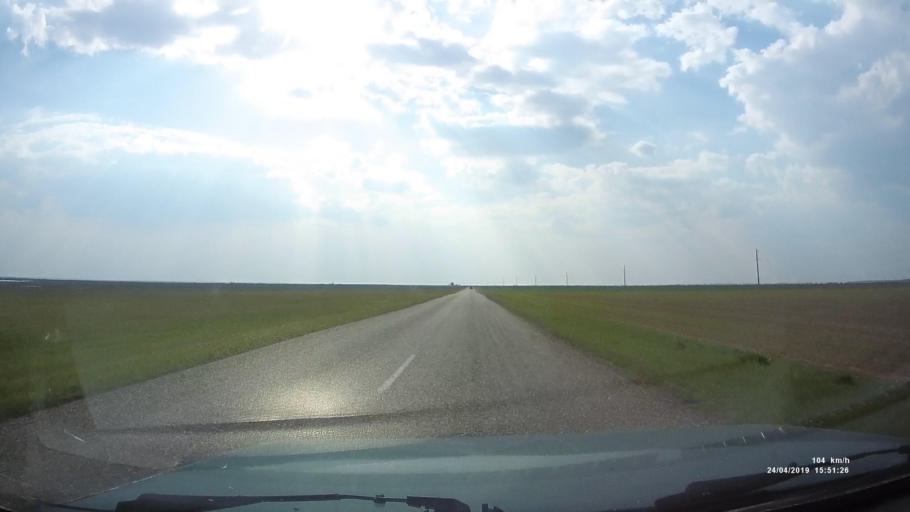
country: RU
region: Kalmykiya
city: Yashalta
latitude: 46.6044
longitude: 42.6107
